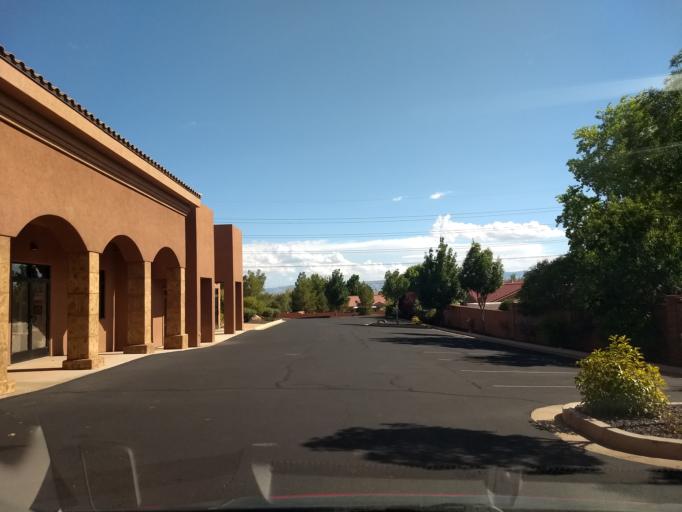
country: US
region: Utah
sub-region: Washington County
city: Santa Clara
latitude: 37.1330
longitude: -113.6142
